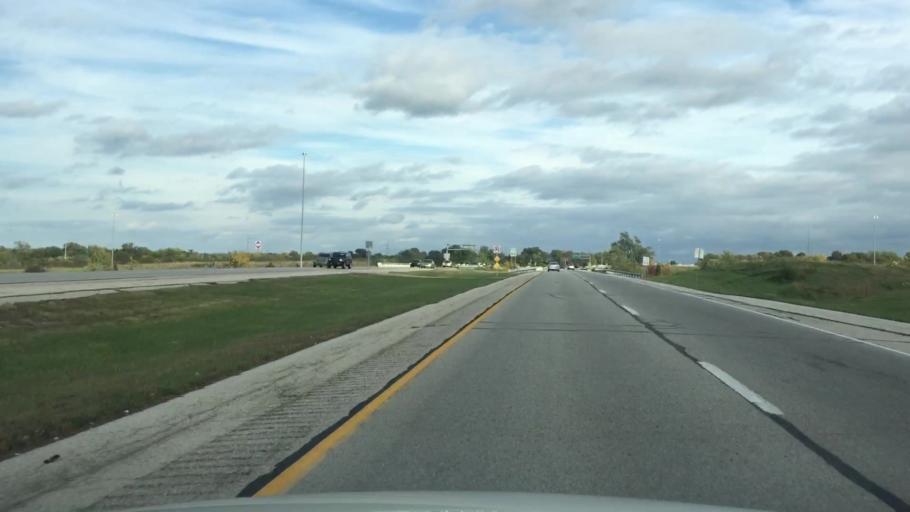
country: US
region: Kansas
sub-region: Wyandotte County
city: Edwardsville
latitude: 39.0105
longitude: -94.7898
